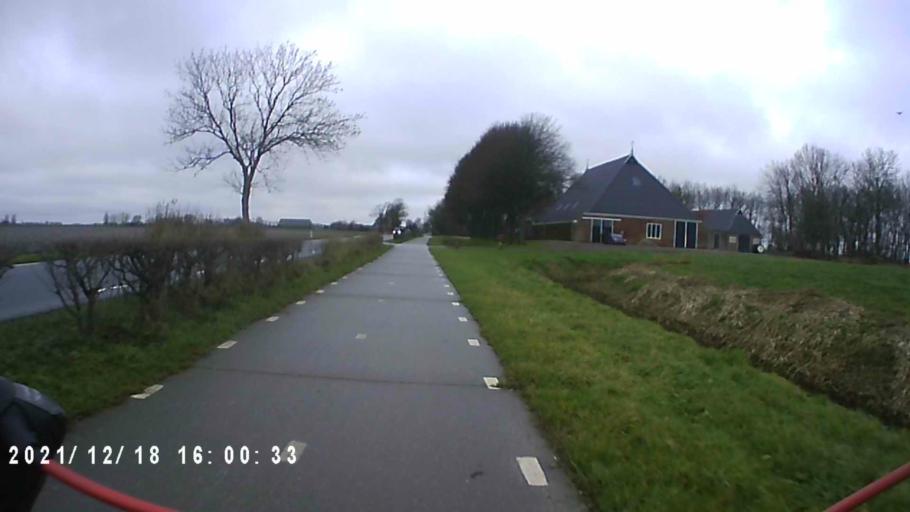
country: NL
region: Friesland
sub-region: Gemeente Dongeradeel
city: Anjum
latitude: 53.3425
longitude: 6.0880
